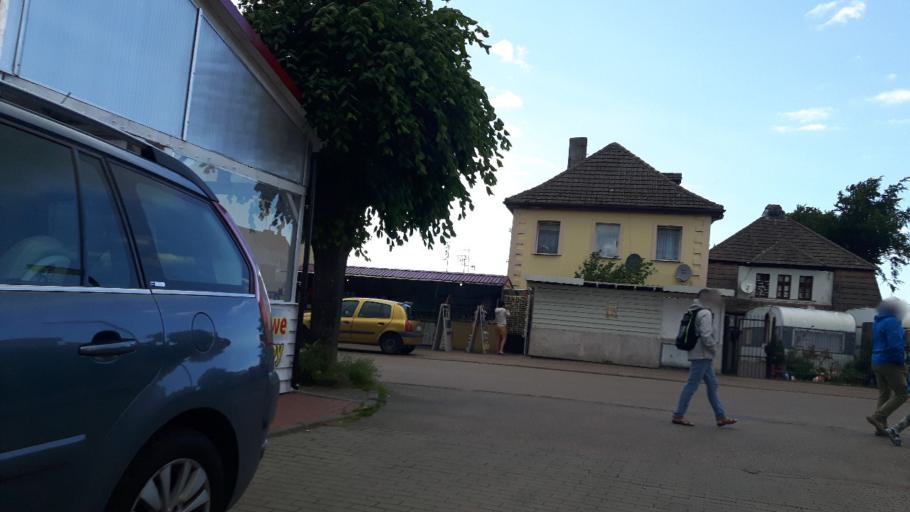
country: PL
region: West Pomeranian Voivodeship
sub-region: Powiat kolobrzeski
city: Ustronie Morskie
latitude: 54.2077
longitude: 15.7241
